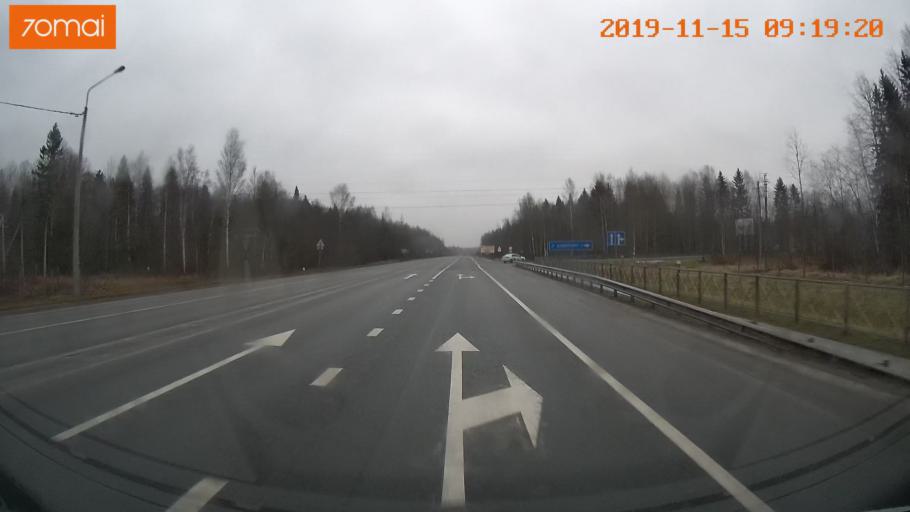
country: RU
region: Vologda
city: Tonshalovo
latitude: 59.2830
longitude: 38.0143
